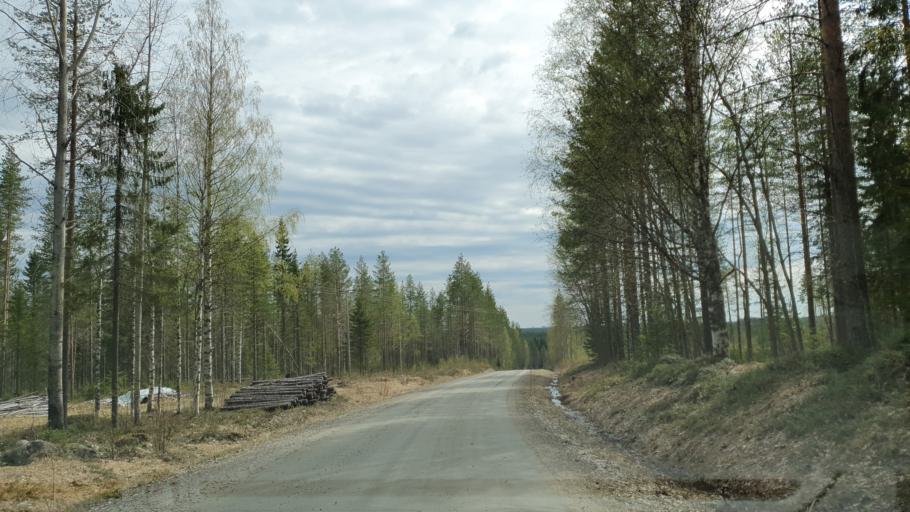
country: FI
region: Kainuu
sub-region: Kehys-Kainuu
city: Kuhmo
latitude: 64.1332
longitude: 29.9740
